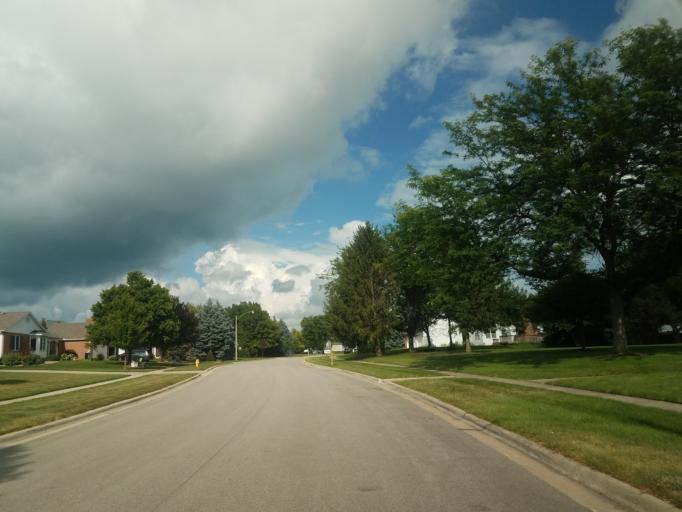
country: US
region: Illinois
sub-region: McLean County
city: Normal
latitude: 40.5074
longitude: -88.9190
